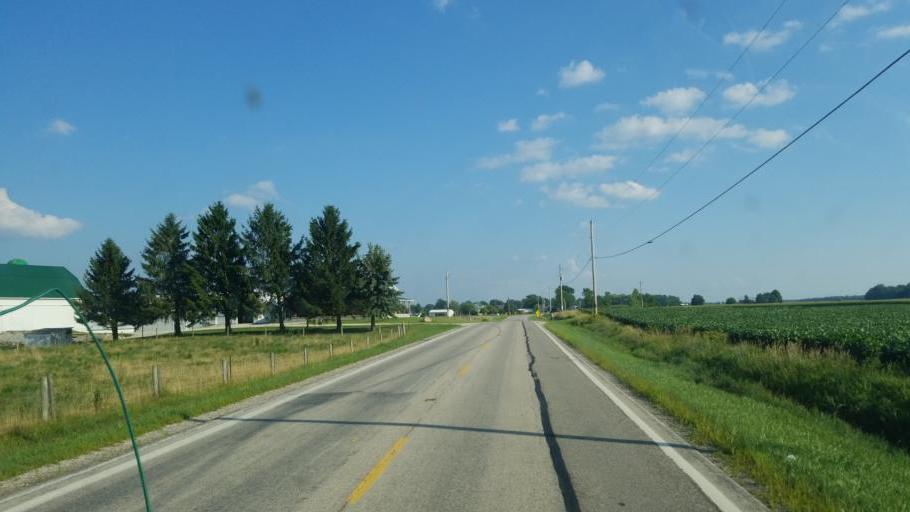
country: US
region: Ohio
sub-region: Crawford County
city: Bucyrus
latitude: 40.8720
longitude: -83.0061
